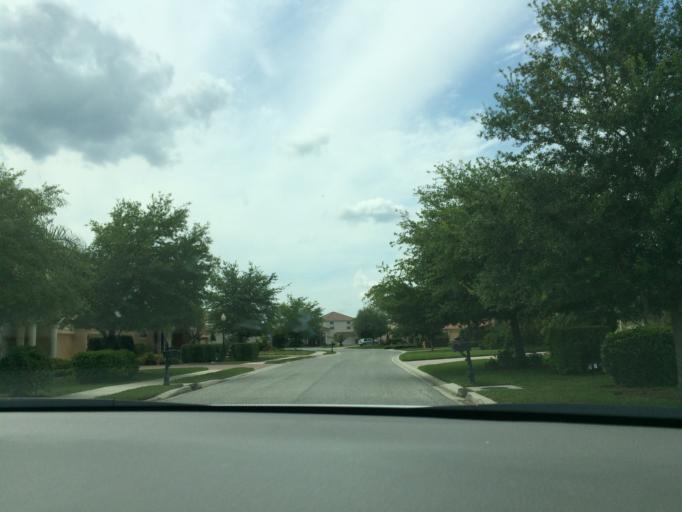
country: US
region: Florida
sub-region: Manatee County
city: Ellenton
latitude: 27.5055
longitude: -82.4120
